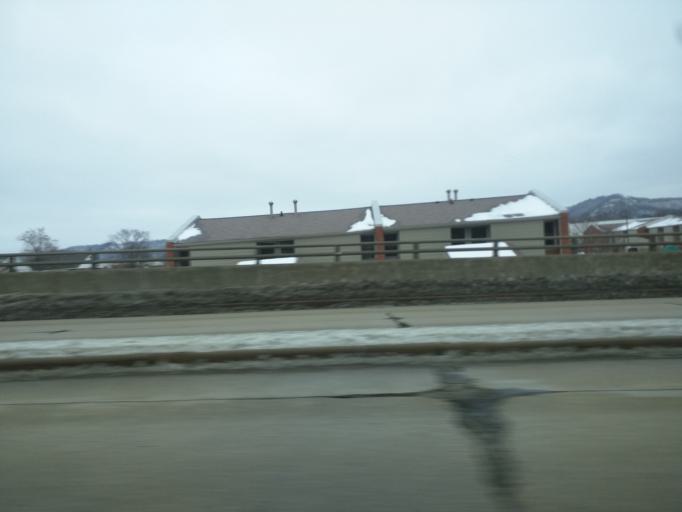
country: US
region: Wisconsin
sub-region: La Crosse County
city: North La Crosse
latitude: 43.8367
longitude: -91.2396
